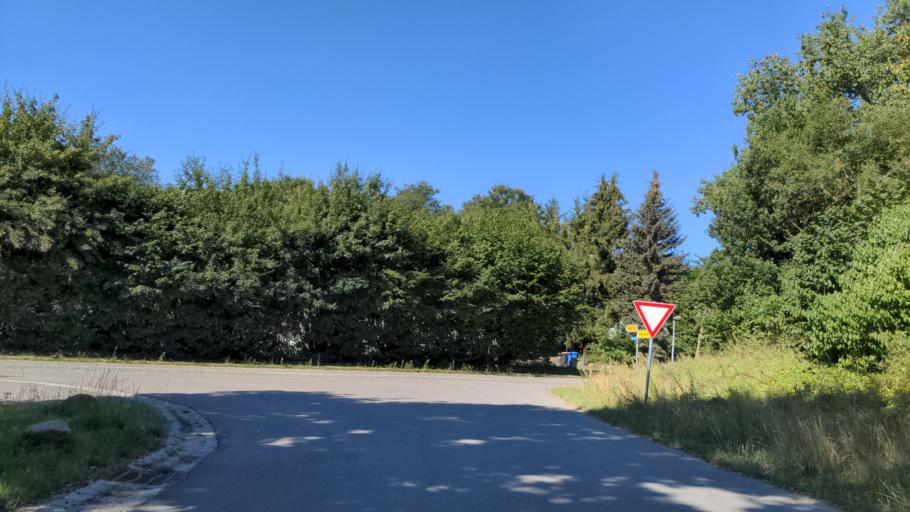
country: DE
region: Mecklenburg-Vorpommern
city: Selmsdorf
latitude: 53.8361
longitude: 10.8693
